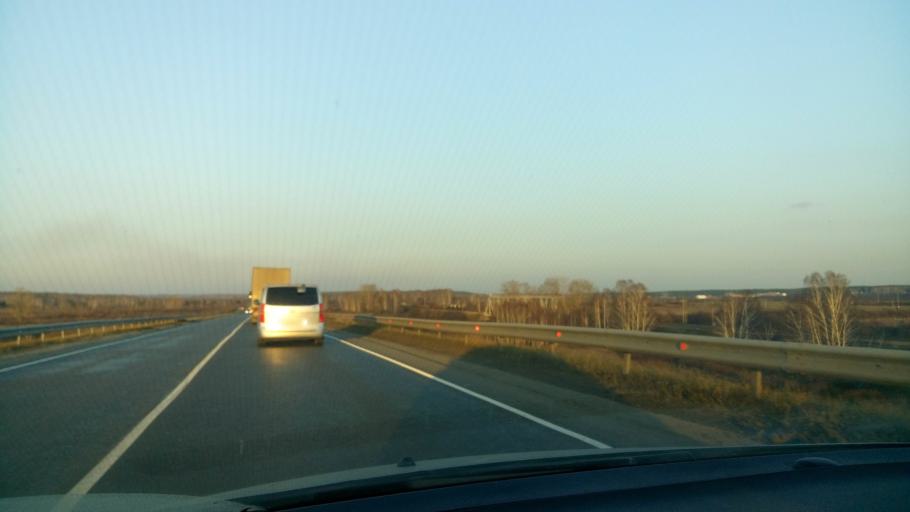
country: RU
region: Sverdlovsk
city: Yelanskiy
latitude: 56.8132
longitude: 62.5344
